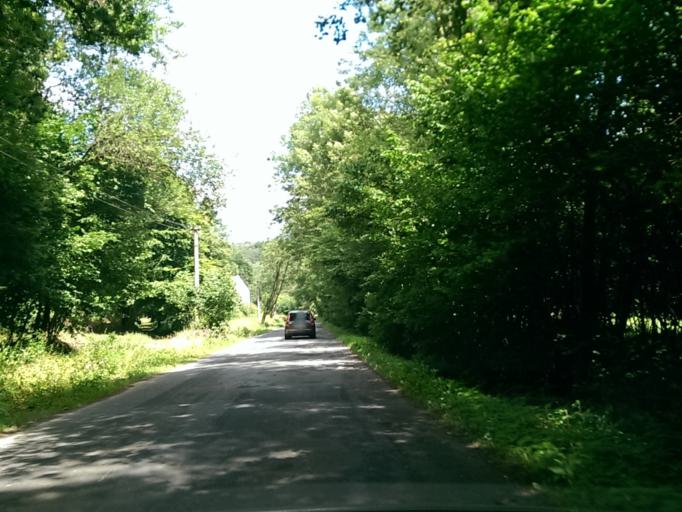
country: CZ
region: Central Bohemia
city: Mseno
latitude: 50.4036
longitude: 14.5656
